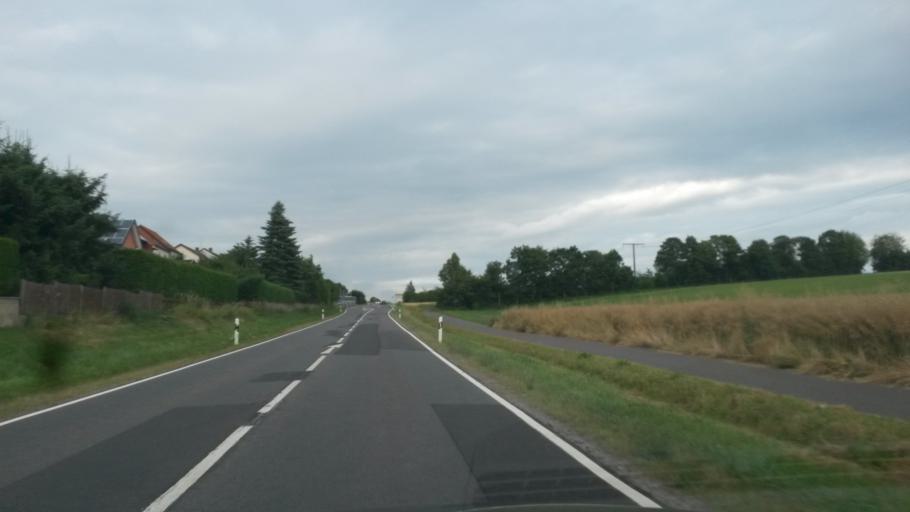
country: DE
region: Bavaria
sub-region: Regierungsbezirk Unterfranken
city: Hettstadt
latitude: 49.7975
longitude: 9.8211
